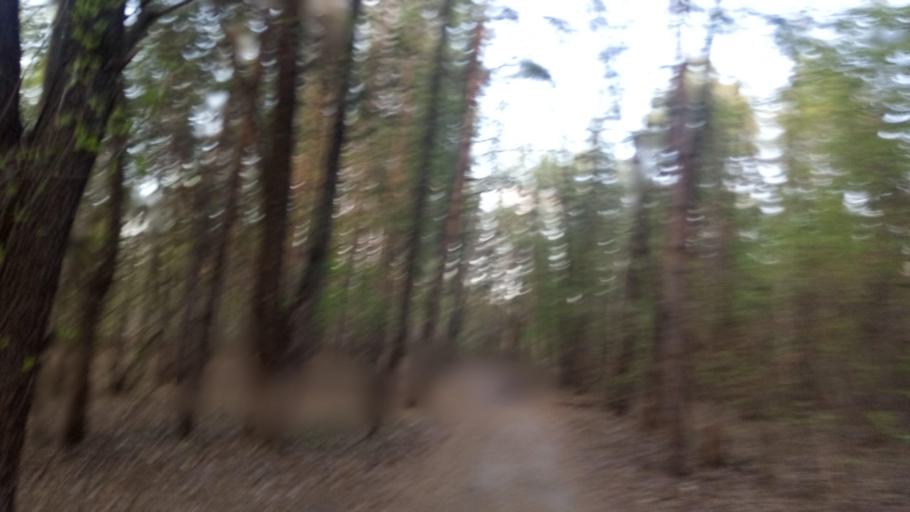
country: RU
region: Chelyabinsk
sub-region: Gorod Chelyabinsk
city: Chelyabinsk
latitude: 55.1664
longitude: 61.3381
